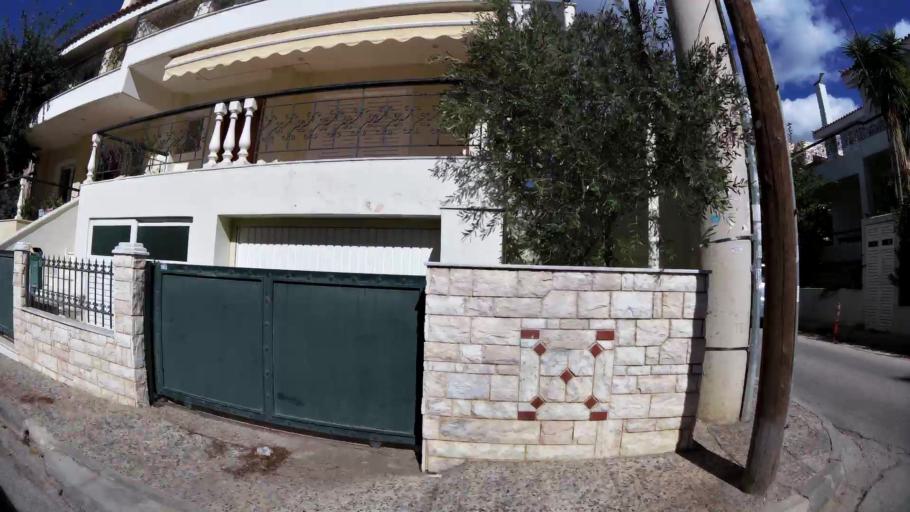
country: GR
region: Attica
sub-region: Nomarchia Anatolikis Attikis
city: Voula
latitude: 37.8368
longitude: 23.7864
